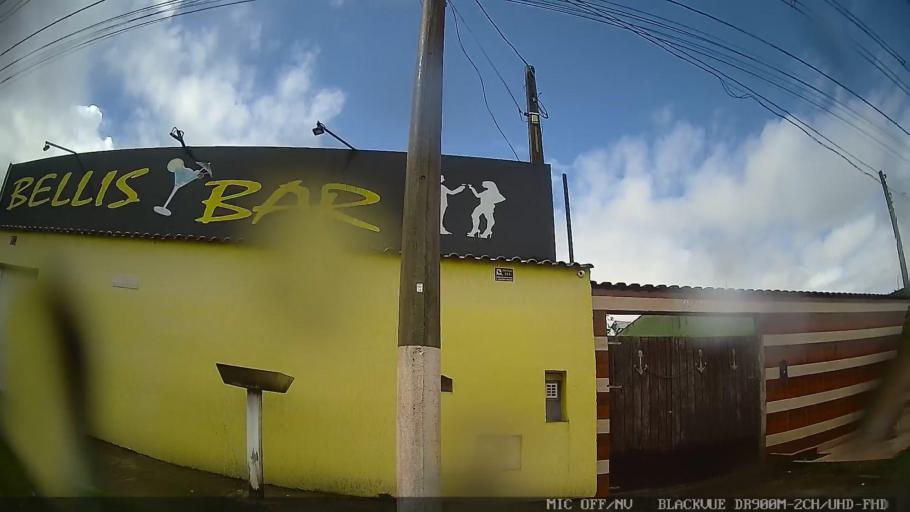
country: BR
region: Sao Paulo
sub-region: Peruibe
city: Peruibe
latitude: -24.2364
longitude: -46.9048
